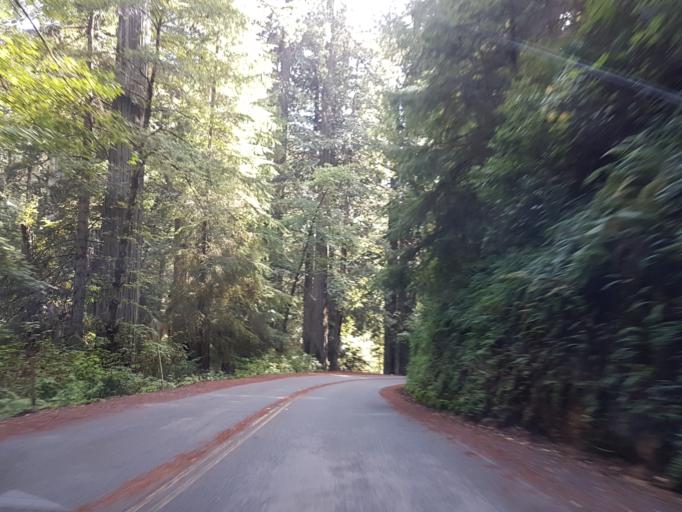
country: US
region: California
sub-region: Del Norte County
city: Bertsch-Oceanview
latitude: 41.4448
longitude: -124.0414
